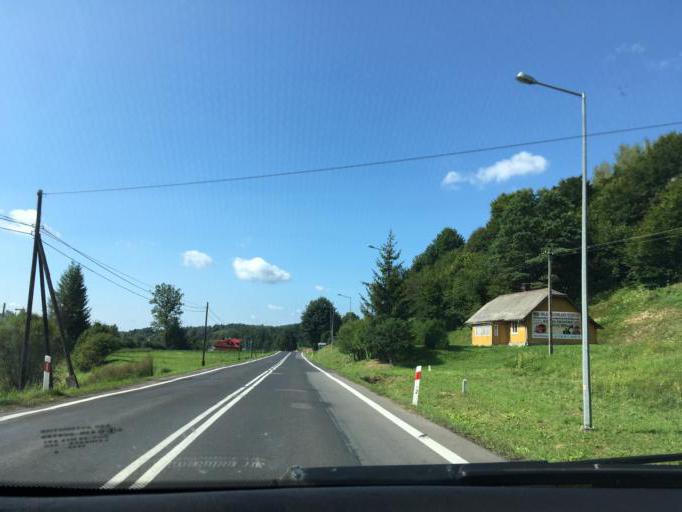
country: PL
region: Subcarpathian Voivodeship
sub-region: Powiat leski
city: Uherce Mineralne
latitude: 49.4707
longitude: 22.4055
